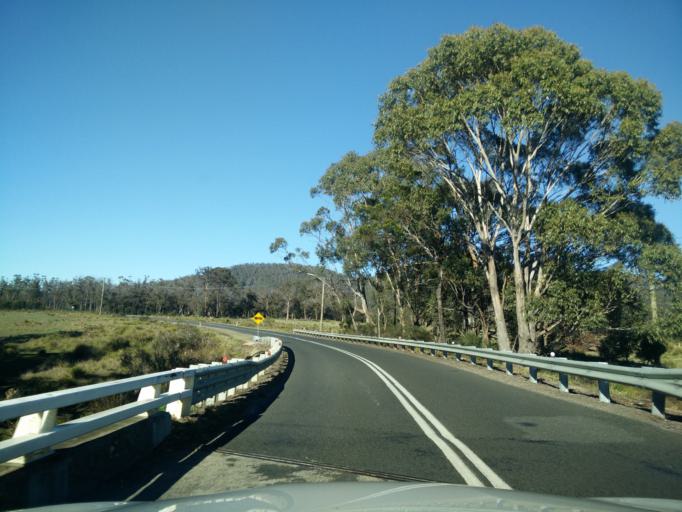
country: AU
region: Tasmania
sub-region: Break O'Day
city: St Helens
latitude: -41.8956
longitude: 148.2571
